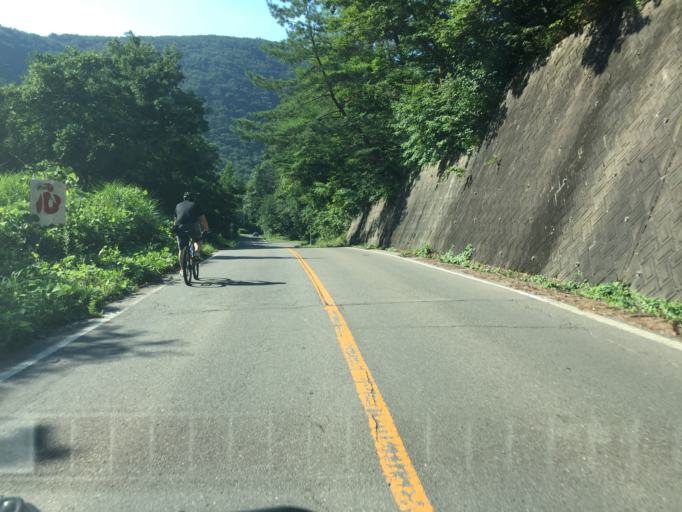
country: JP
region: Fukushima
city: Fukushima-shi
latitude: 37.8591
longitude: 140.4352
